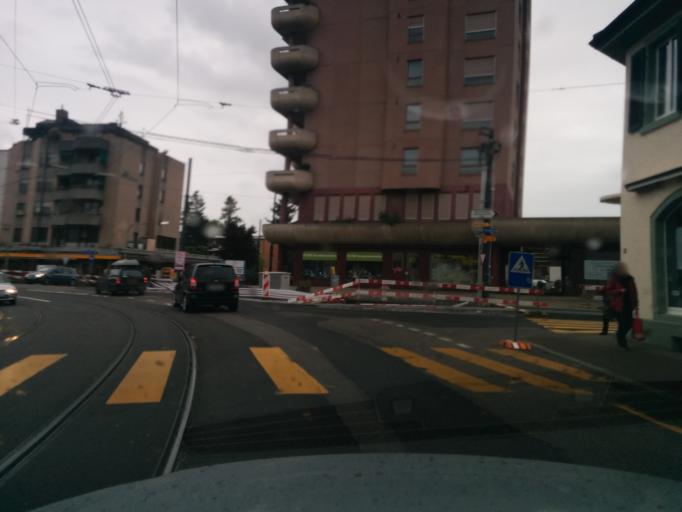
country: CH
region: Basel-Landschaft
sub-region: Bezirk Arlesheim
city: Aesch
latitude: 47.4932
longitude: 7.5899
